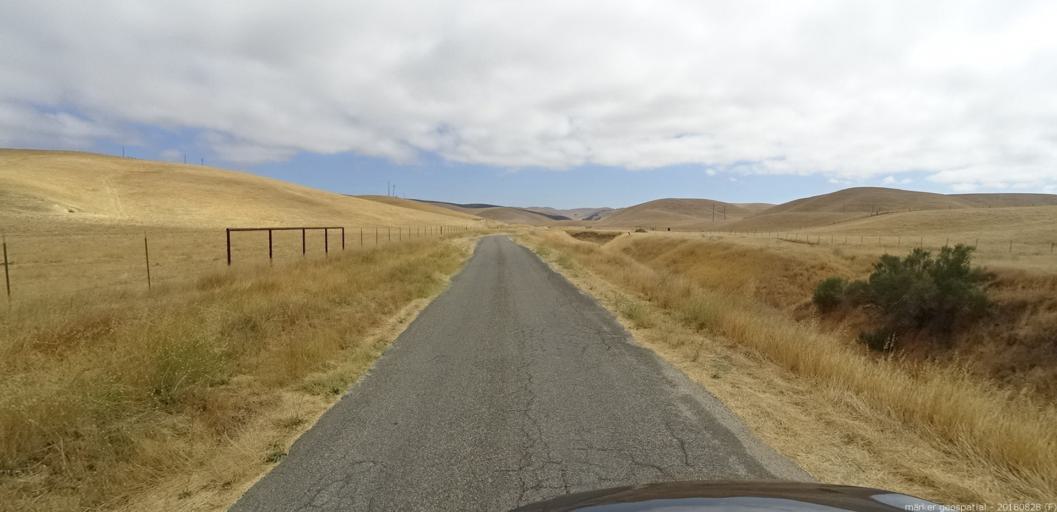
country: US
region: California
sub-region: San Luis Obispo County
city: Lake Nacimiento
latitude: 35.9766
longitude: -120.8622
